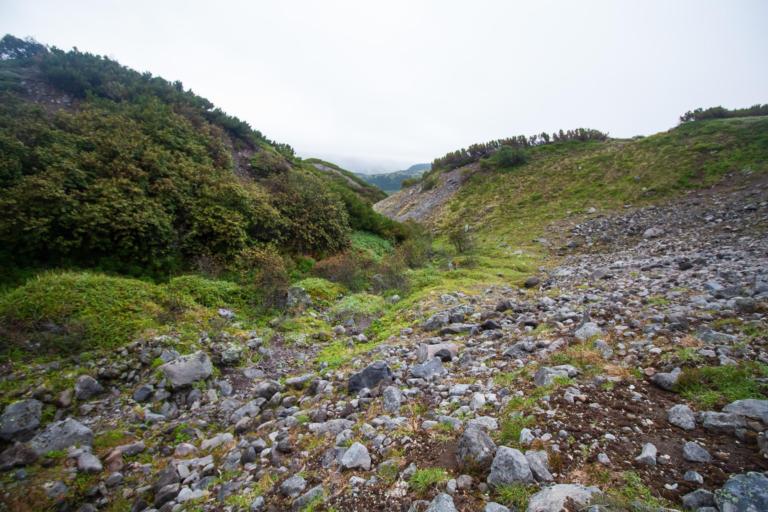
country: RU
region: Kamtsjatka
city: Yelizovo
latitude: 53.9198
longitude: 158.0409
